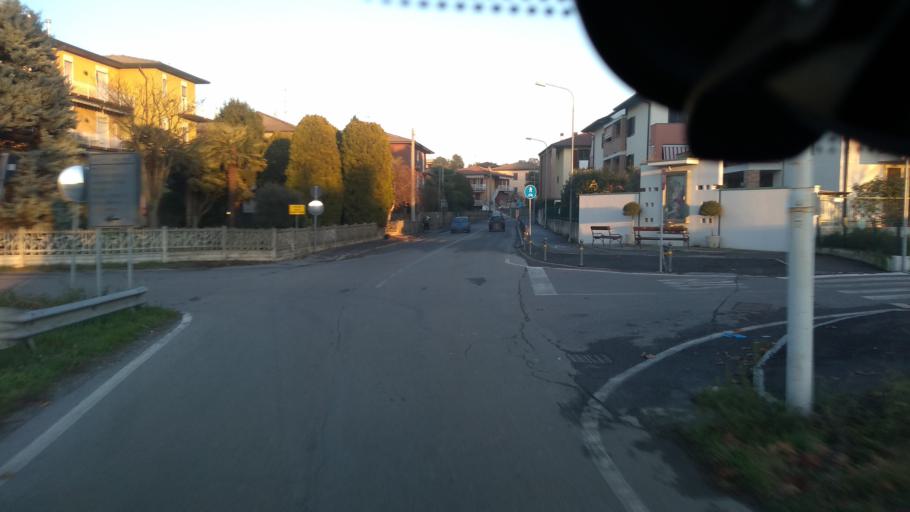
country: IT
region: Lombardy
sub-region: Provincia di Bergamo
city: Casirate d'Adda
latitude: 45.4954
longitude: 9.5636
